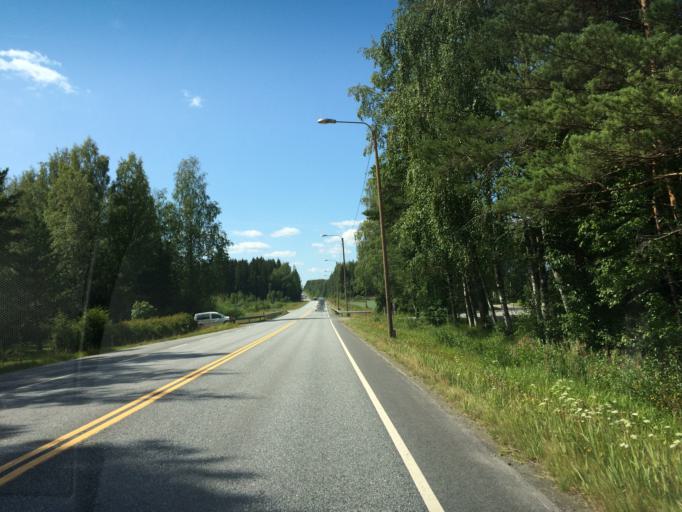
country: FI
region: Pirkanmaa
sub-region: Lounais-Pirkanmaa
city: Kiikoinen
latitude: 61.4818
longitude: 22.6175
